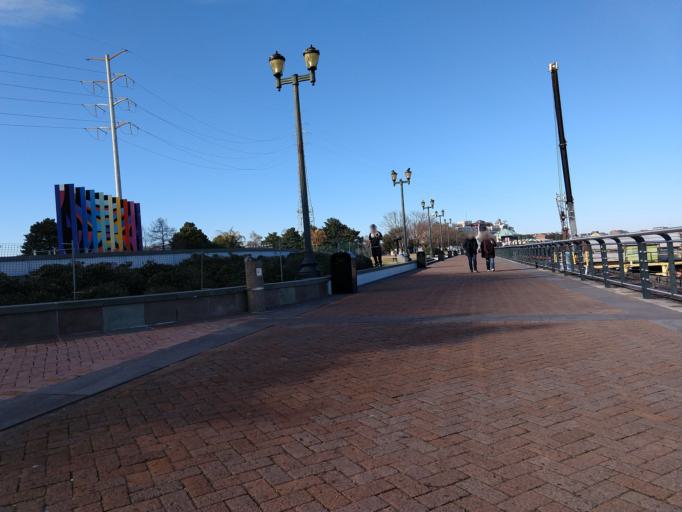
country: US
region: Louisiana
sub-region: Orleans Parish
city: New Orleans
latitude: 29.9522
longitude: -90.0627
